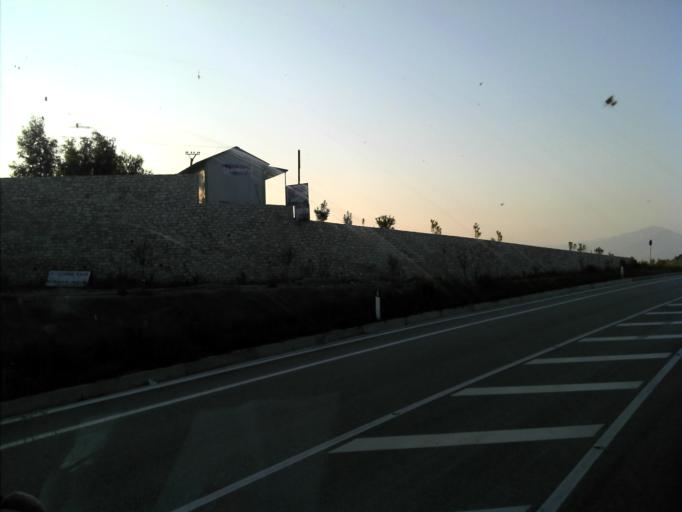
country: AL
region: Fier
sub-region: Rrethi i Mallakastres
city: Fratar
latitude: 40.4916
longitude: 19.8399
